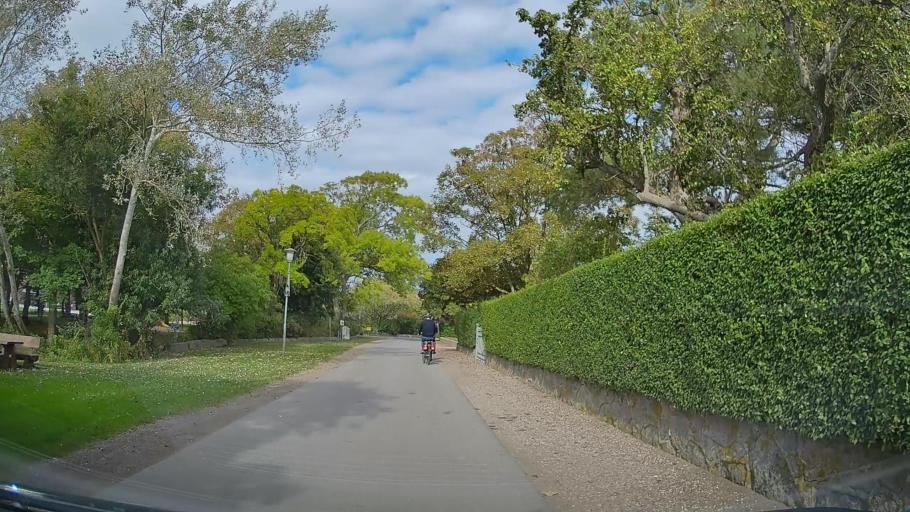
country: DE
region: Schleswig-Holstein
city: Grossenbrode
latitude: 54.5212
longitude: 11.0540
